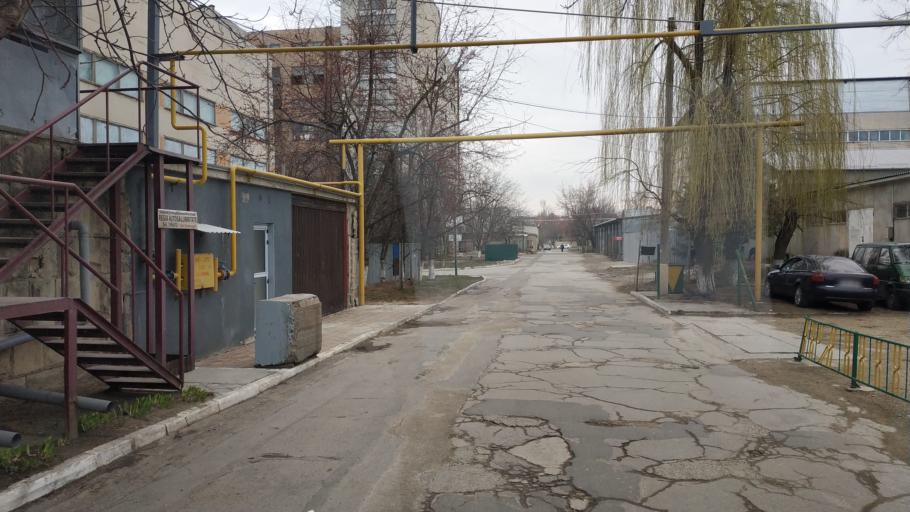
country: MD
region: Chisinau
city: Vatra
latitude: 47.0347
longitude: 28.7719
